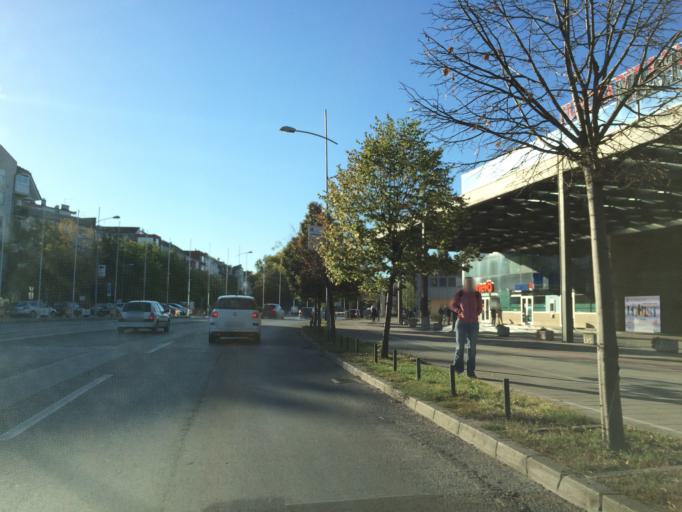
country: RS
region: Autonomna Pokrajina Vojvodina
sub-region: Juznobacki Okrug
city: Novi Sad
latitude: 45.2583
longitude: 19.8236
